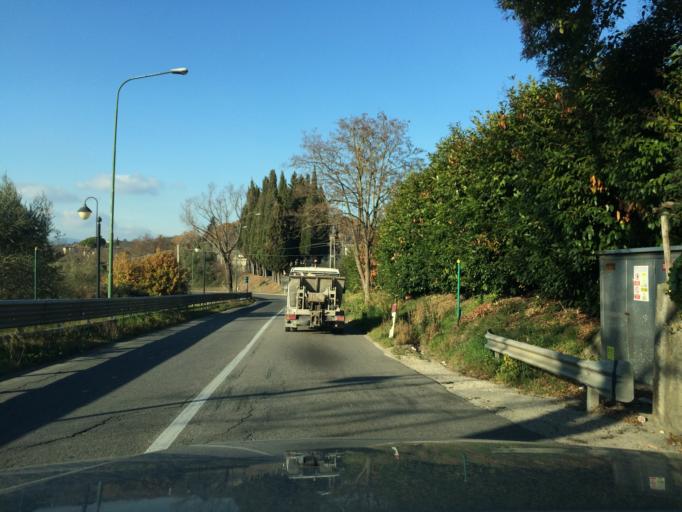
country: IT
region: Umbria
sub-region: Provincia di Terni
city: Fornole
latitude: 42.5440
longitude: 12.4534
